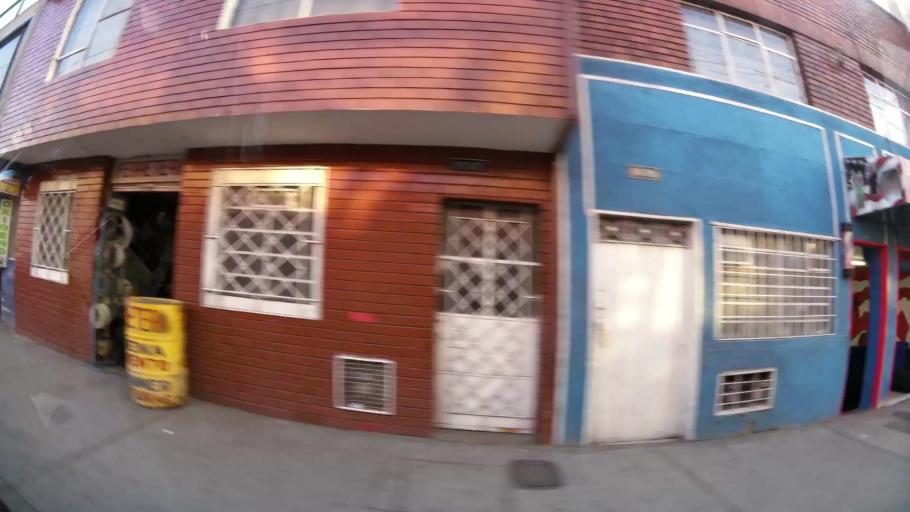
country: CO
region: Bogota D.C.
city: Bogota
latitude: 4.5649
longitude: -74.1301
